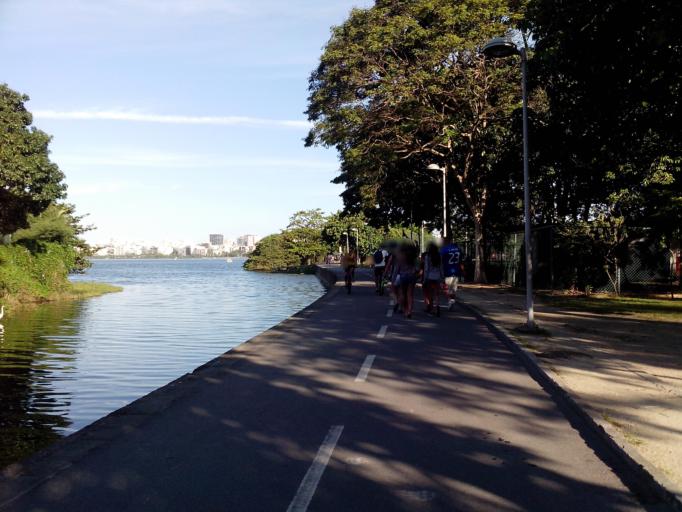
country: BR
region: Rio de Janeiro
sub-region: Rio De Janeiro
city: Rio de Janeiro
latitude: -22.9687
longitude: -43.2171
